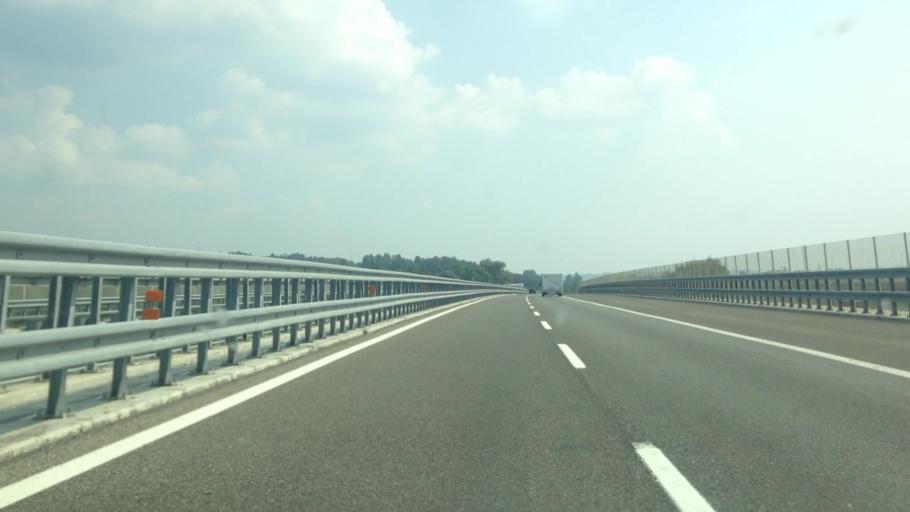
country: IT
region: Piedmont
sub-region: Provincia di Asti
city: Asti
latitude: 44.9135
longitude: 8.2268
